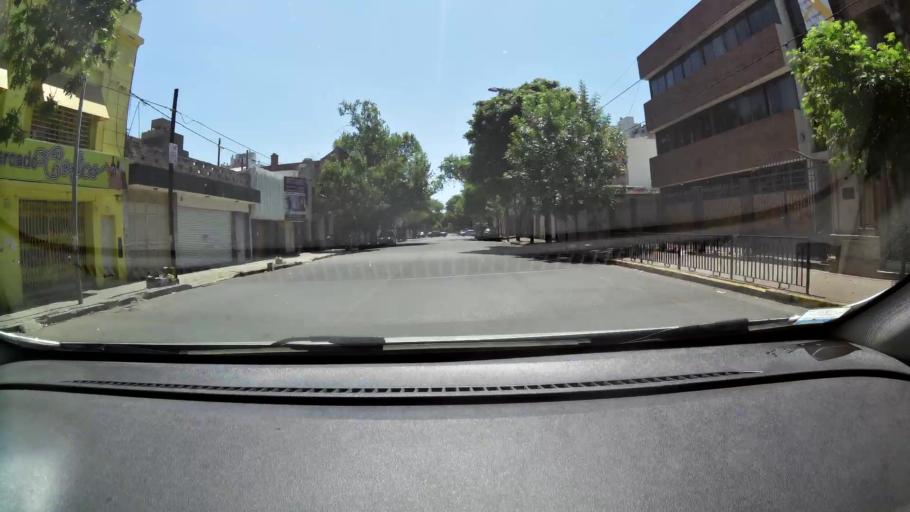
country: AR
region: Cordoba
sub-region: Departamento de Capital
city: Cordoba
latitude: -31.3964
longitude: -64.1879
